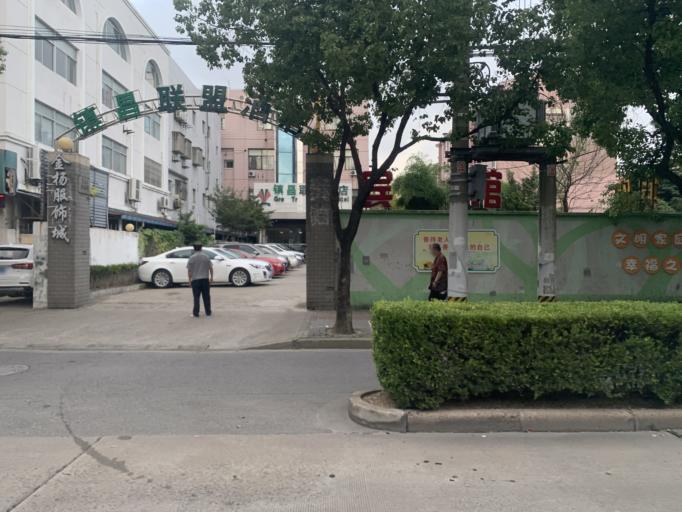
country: CN
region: Shanghai Shi
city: Pudong
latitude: 31.2519
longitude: 121.5774
